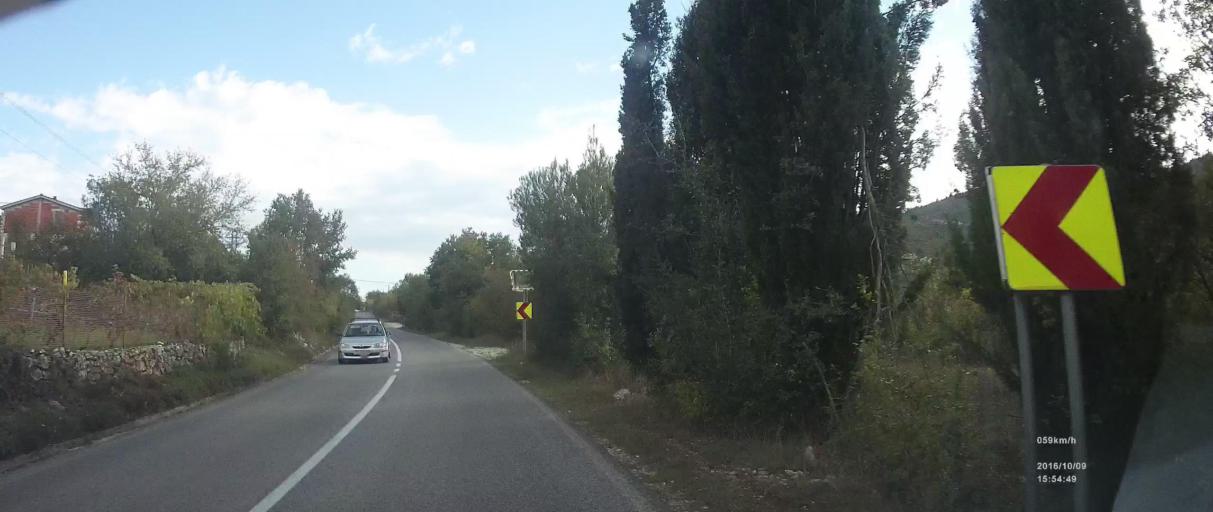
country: HR
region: Splitsko-Dalmatinska
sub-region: Grad Trogir
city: Trogir
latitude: 43.5915
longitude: 16.2262
